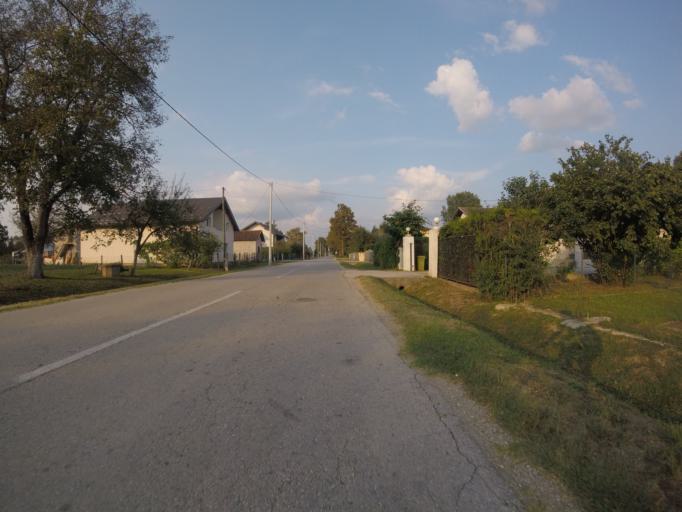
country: HR
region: Zagrebacka
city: Kuce
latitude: 45.7150
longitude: 16.1947
